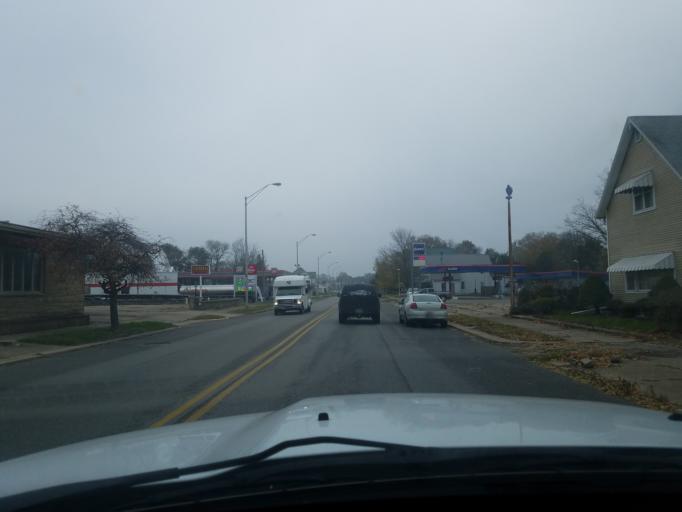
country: US
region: Indiana
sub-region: Cass County
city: Logansport
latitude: 40.7518
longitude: -86.3736
